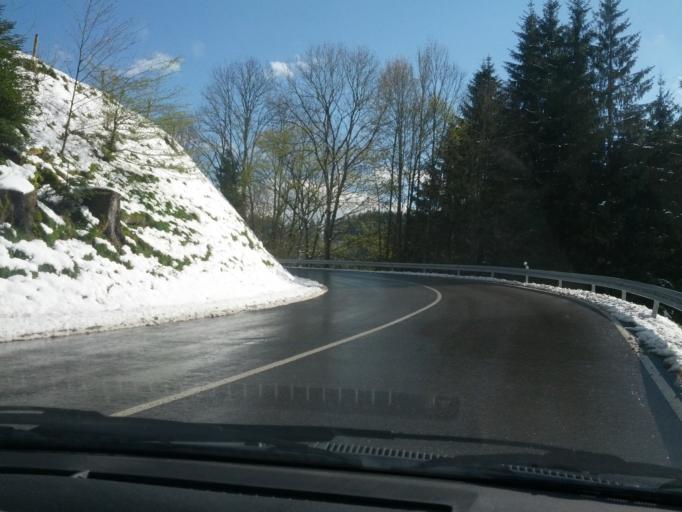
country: DE
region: Baden-Wuerttemberg
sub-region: Freiburg Region
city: Sankt Peter
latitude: 48.0269
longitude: 8.0281
